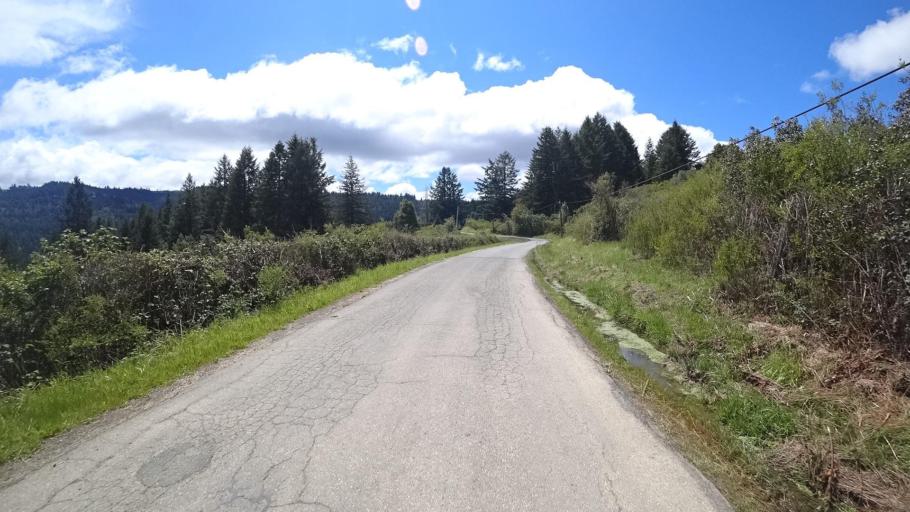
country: US
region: California
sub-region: Humboldt County
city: Blue Lake
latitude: 40.7663
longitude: -123.9403
